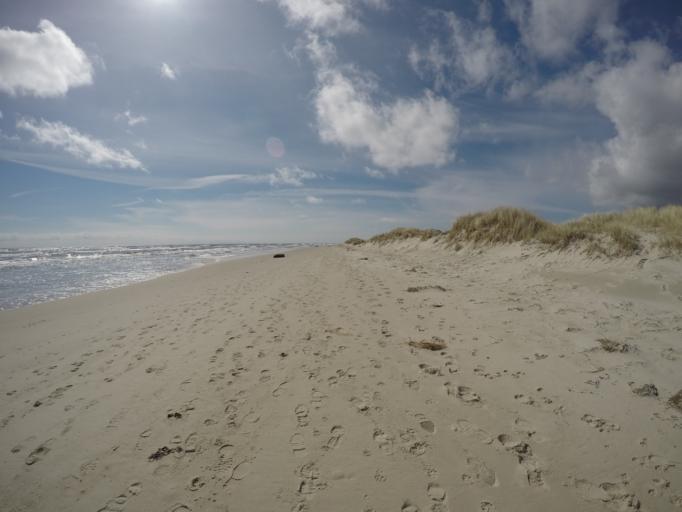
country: SE
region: Skane
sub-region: Simrishamns Kommun
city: Simrishamn
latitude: 55.3972
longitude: 14.2125
